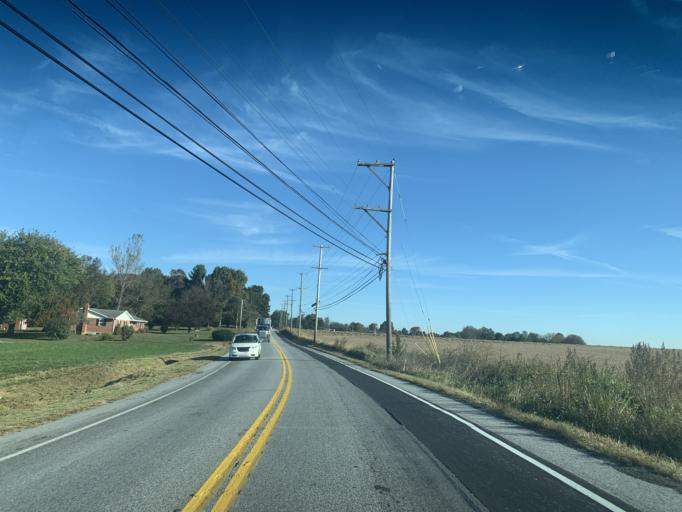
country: US
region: Pennsylvania
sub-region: Chester County
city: Oxford
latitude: 39.8536
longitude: -75.9332
